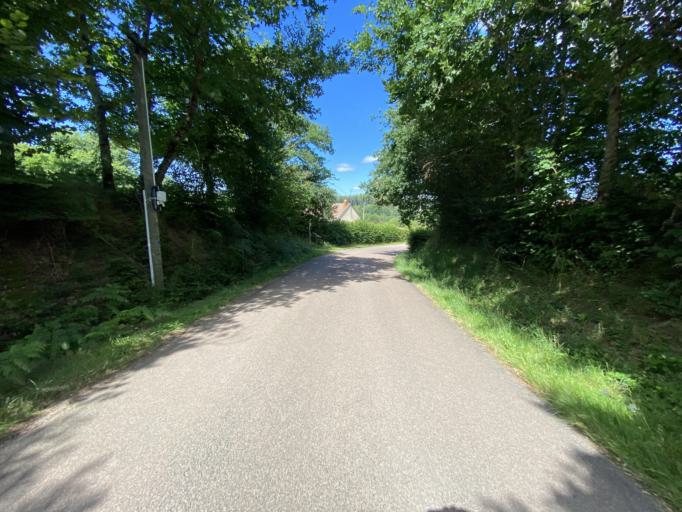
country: FR
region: Bourgogne
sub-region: Departement de la Cote-d'Or
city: Saulieu
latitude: 47.3233
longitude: 4.1536
